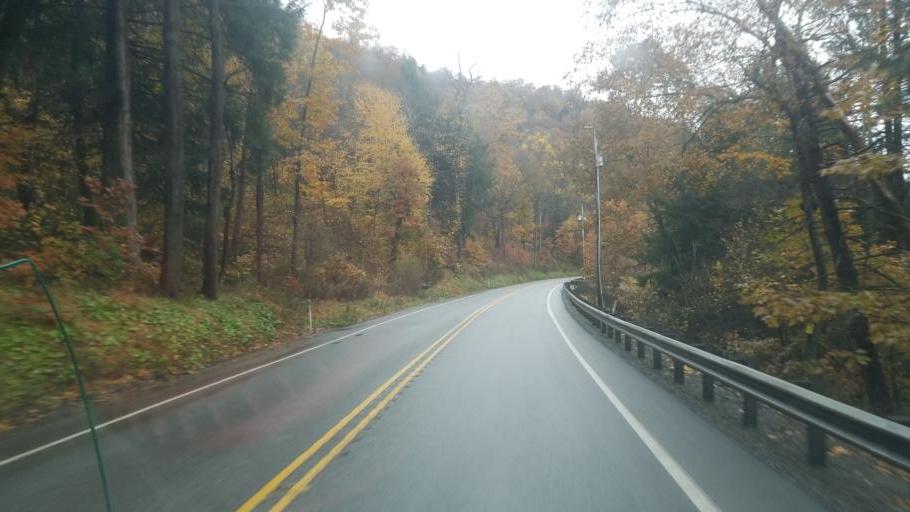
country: US
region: Pennsylvania
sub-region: Clearfield County
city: Clearfield
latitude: 41.0557
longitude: -78.3782
